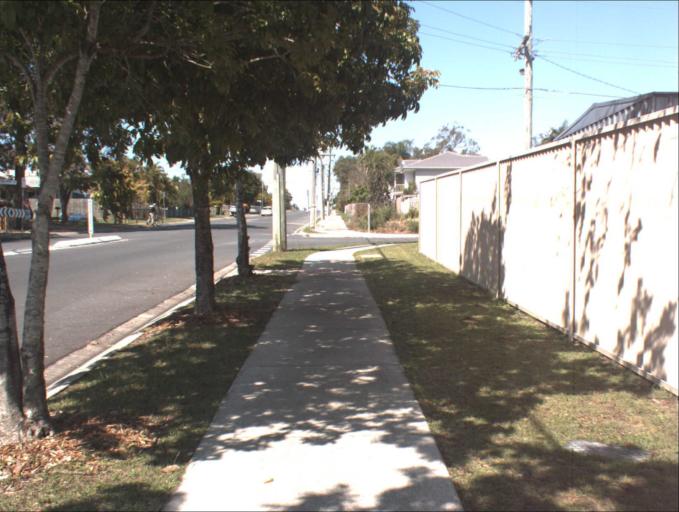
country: AU
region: Queensland
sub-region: Logan
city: Logan City
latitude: -27.6745
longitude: 153.0942
